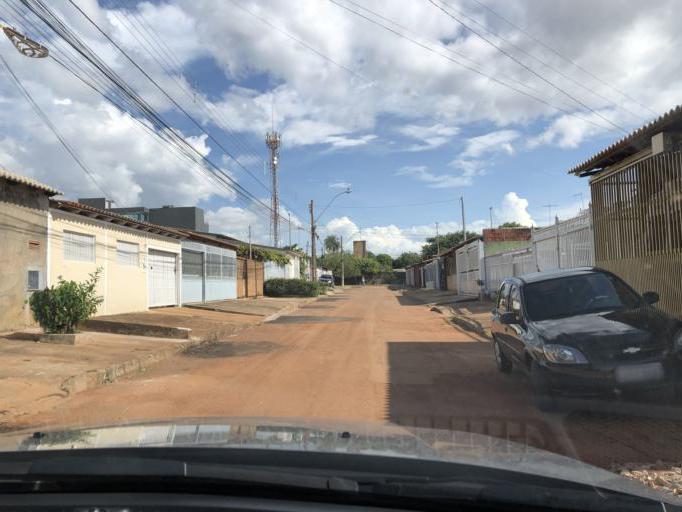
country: BR
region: Federal District
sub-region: Brasilia
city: Brasilia
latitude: -15.7957
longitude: -48.1226
